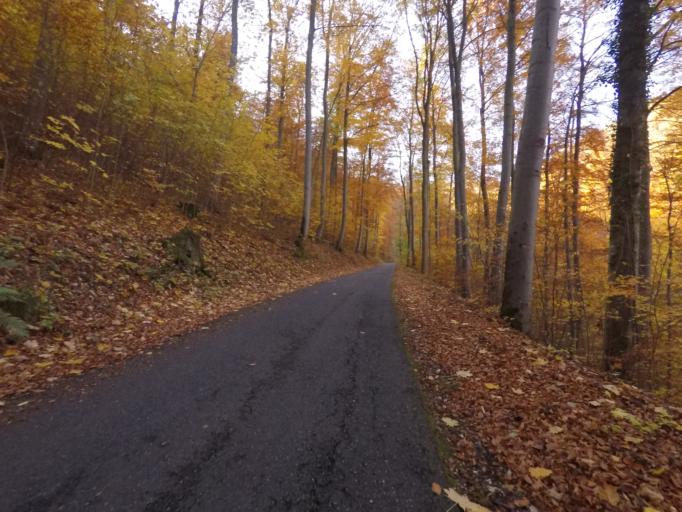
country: DE
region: Baden-Wuerttemberg
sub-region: Tuebingen Region
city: Pfullingen
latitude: 48.4371
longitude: 9.2351
